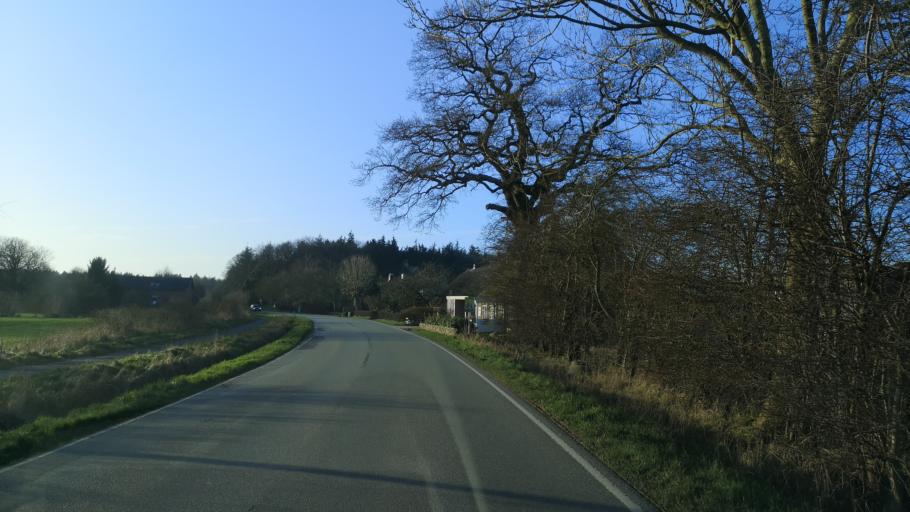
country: DE
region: Schleswig-Holstein
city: Ausacker
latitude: 54.6968
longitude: 9.5675
